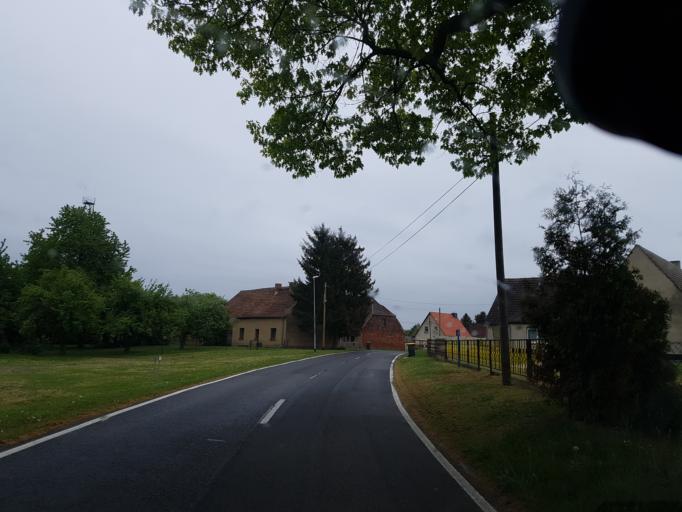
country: DE
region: Brandenburg
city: Spremberg
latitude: 51.6534
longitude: 14.3263
